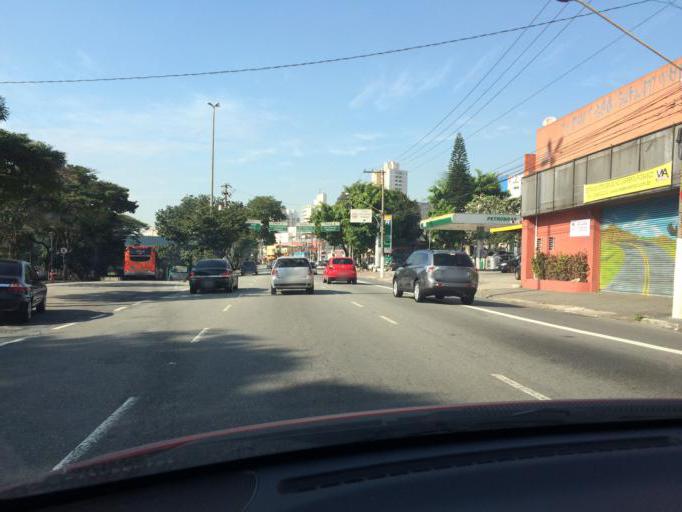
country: BR
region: Sao Paulo
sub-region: Osasco
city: Osasco
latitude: -23.5458
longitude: -46.7623
